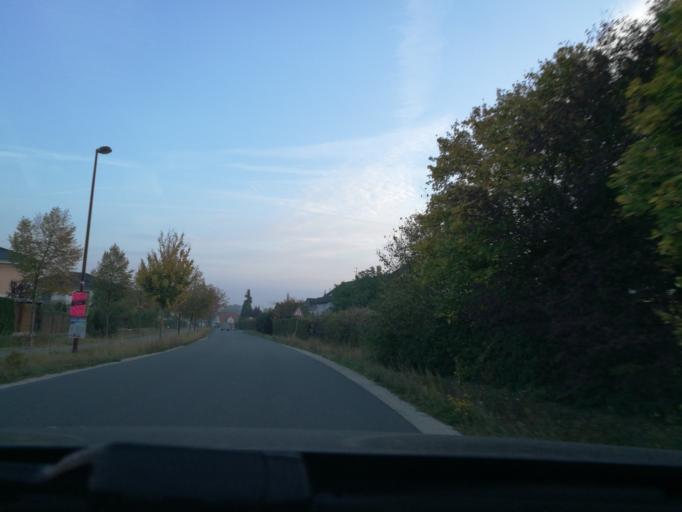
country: DE
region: Bavaria
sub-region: Regierungsbezirk Mittelfranken
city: Obermichelbach
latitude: 49.5265
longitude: 10.9060
